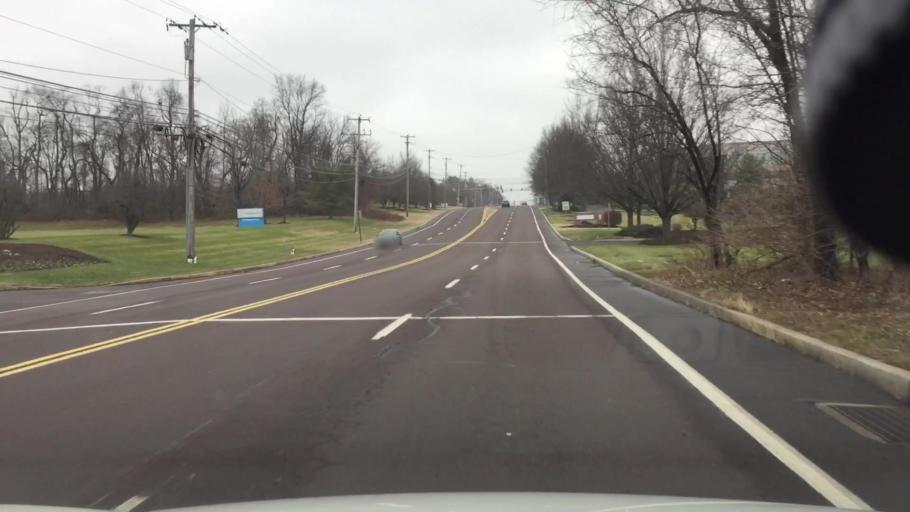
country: US
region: Pennsylvania
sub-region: Montgomery County
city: Horsham
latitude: 40.1665
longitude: -75.1466
